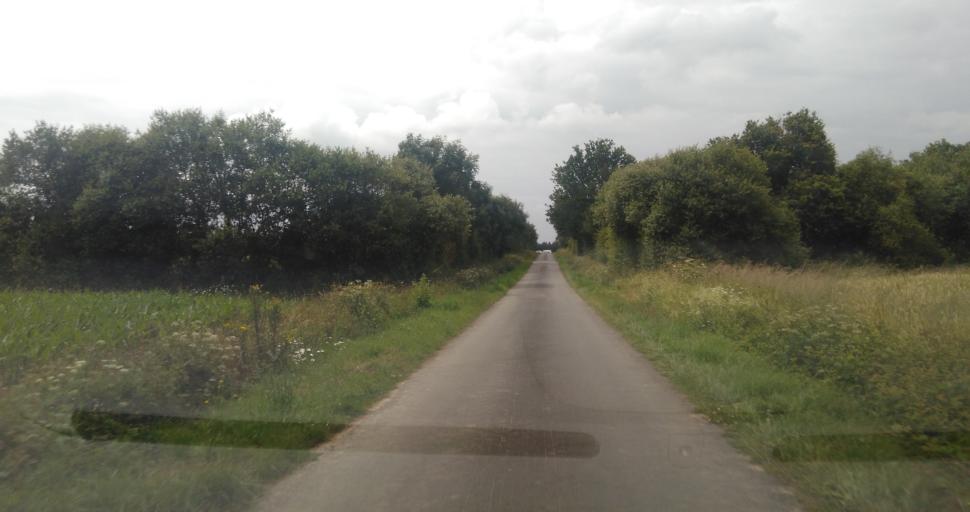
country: FR
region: Pays de la Loire
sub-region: Departement de la Vendee
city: Saint-Georges-de-Montaigu
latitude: 46.9291
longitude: -1.3208
